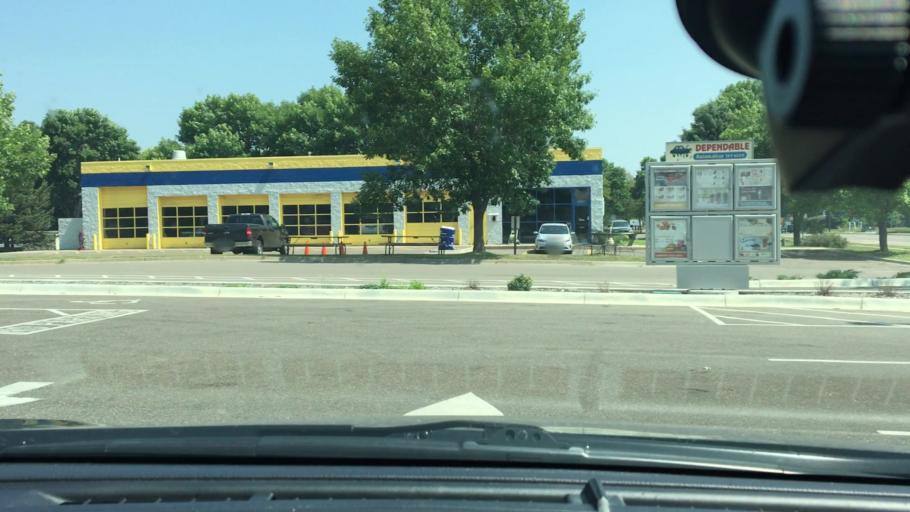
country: US
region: Minnesota
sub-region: Hennepin County
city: Osseo
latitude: 45.1093
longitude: -93.3866
